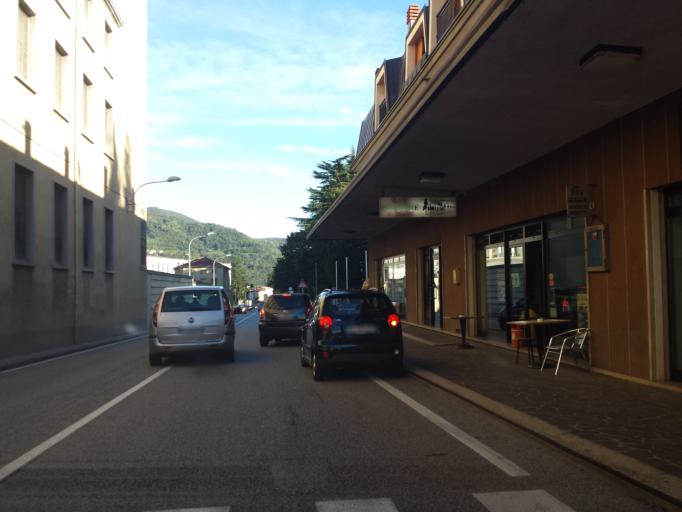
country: IT
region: Veneto
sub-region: Provincia di Vicenza
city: San Quirico
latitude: 45.6647
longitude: 11.2901
